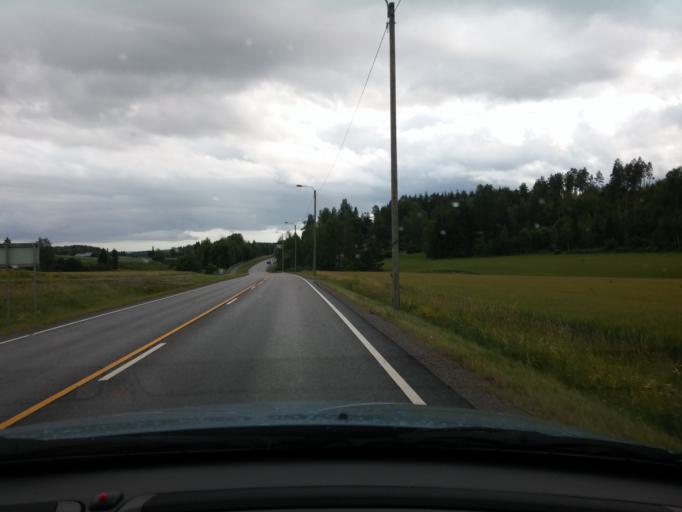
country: FI
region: Uusimaa
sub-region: Porvoo
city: Askola
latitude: 60.5196
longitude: 25.5790
